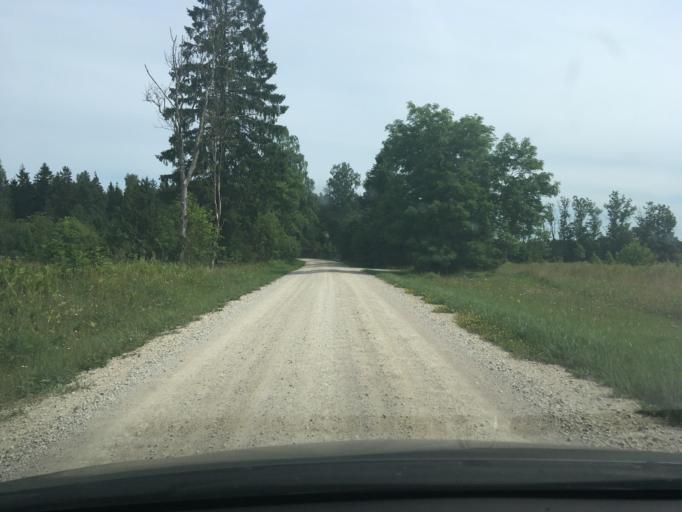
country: EE
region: Raplamaa
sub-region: Maerjamaa vald
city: Marjamaa
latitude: 58.9456
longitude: 24.5551
